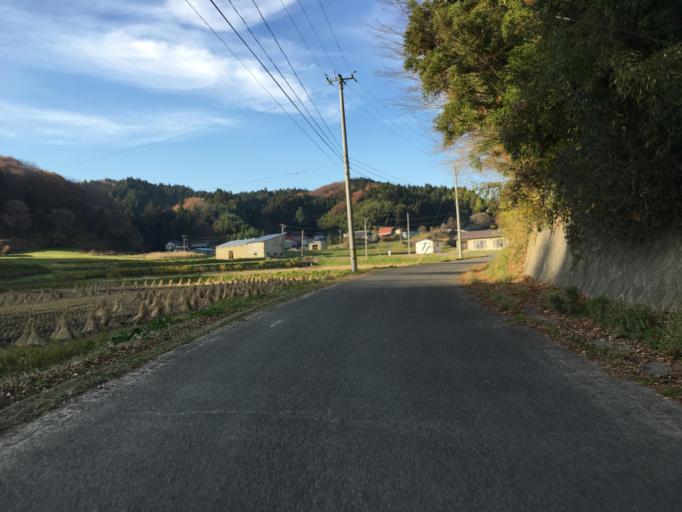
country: JP
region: Fukushima
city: Ishikawa
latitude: 37.2384
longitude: 140.5887
